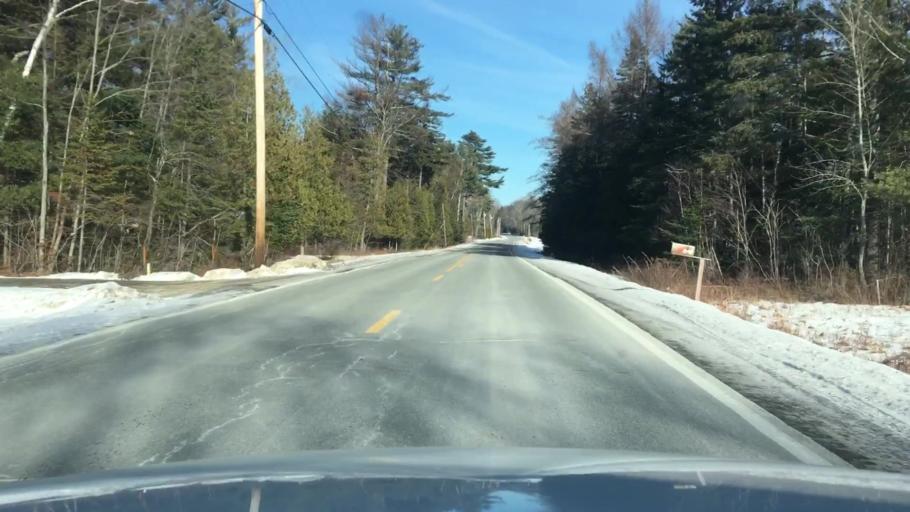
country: US
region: Maine
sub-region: Hancock County
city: Orland
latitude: 44.6166
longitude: -68.7198
